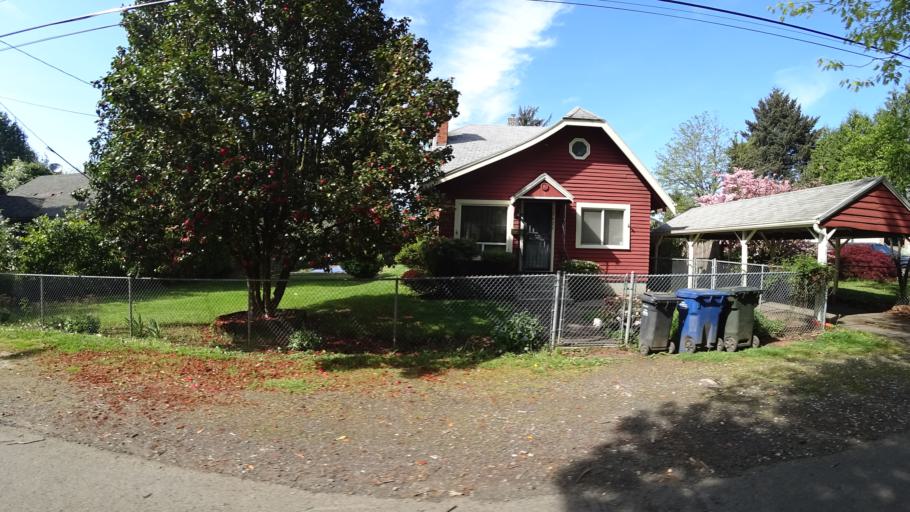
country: US
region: Oregon
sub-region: Clackamas County
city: Milwaukie
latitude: 45.4578
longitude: -122.6276
